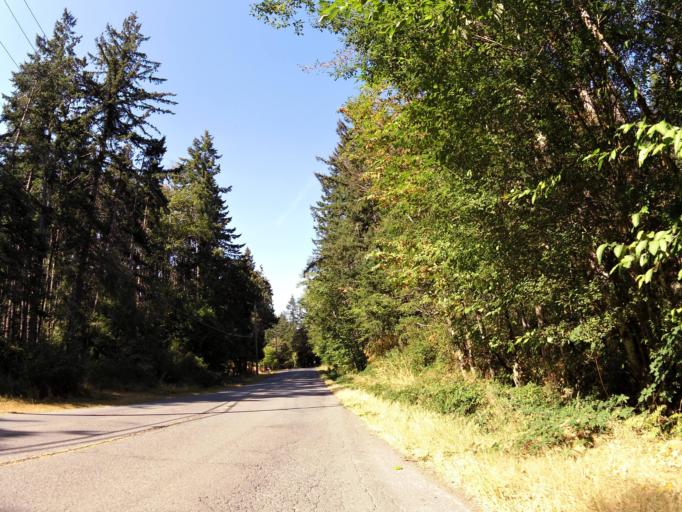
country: CA
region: British Columbia
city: North Saanich
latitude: 48.6813
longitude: -123.5507
